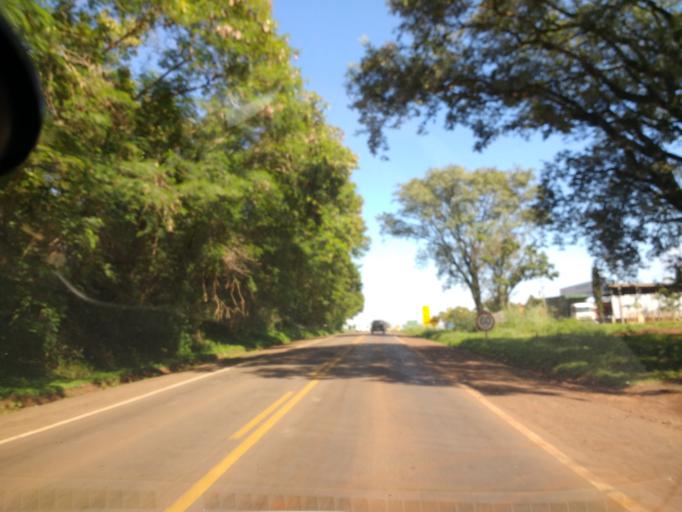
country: BR
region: Parana
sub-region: Terra Boa
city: Terra Boa
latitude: -23.6310
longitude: -52.4607
